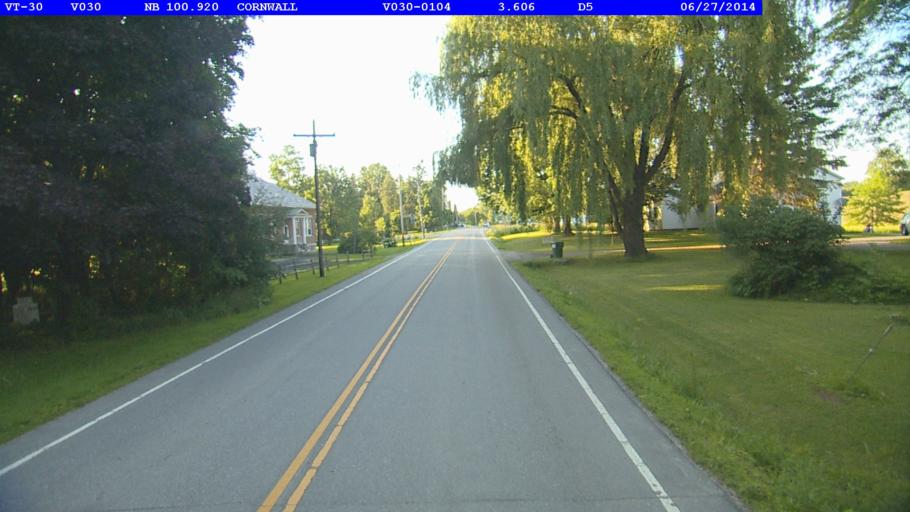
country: US
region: Vermont
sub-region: Addison County
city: Middlebury (village)
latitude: 43.9597
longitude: -73.2098
